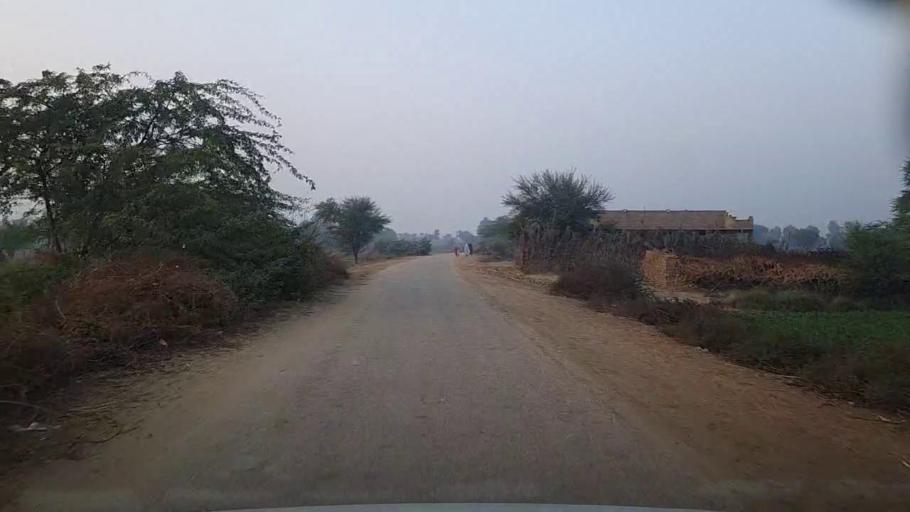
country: PK
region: Sindh
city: Bozdar
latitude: 27.0584
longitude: 68.5951
